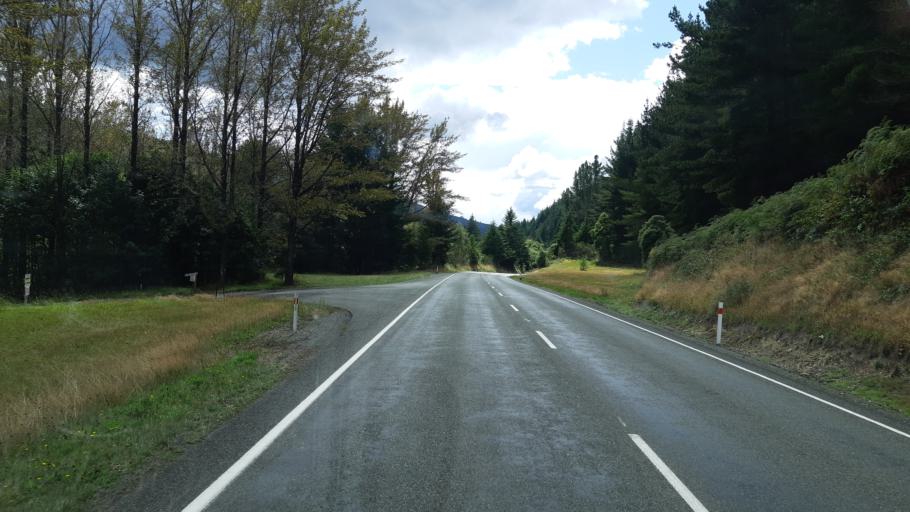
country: NZ
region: Tasman
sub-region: Tasman District
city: Wakefield
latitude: -41.5870
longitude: 172.7650
